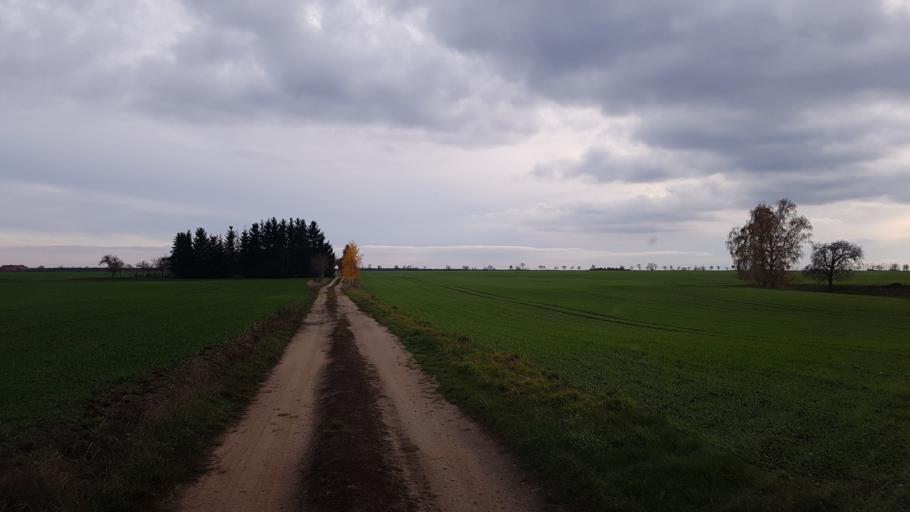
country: DE
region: Brandenburg
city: Schlieben
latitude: 51.6676
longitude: 13.4192
